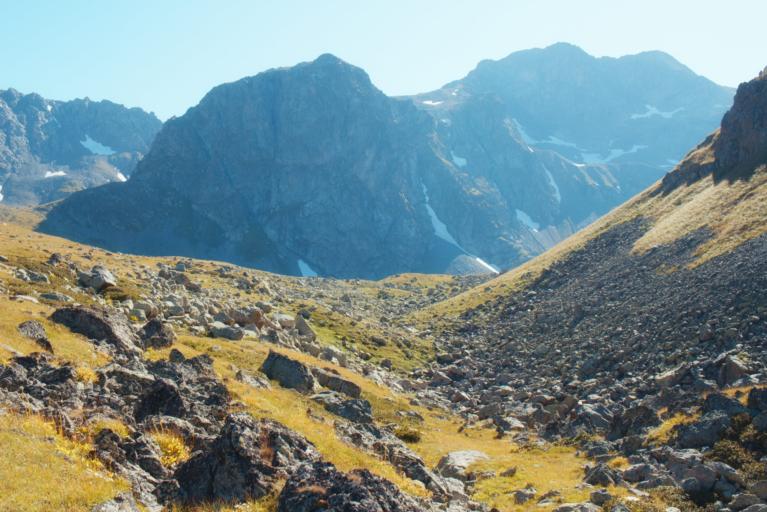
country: RU
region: Karachayevo-Cherkesiya
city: Mednogorskiy
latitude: 43.6127
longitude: 41.1406
